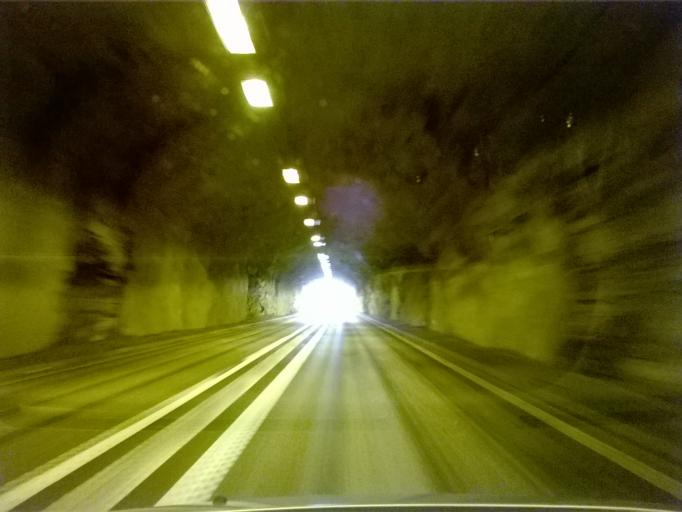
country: SE
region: Vaestra Goetaland
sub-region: Orust
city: Henan
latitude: 58.3009
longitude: 11.7002
